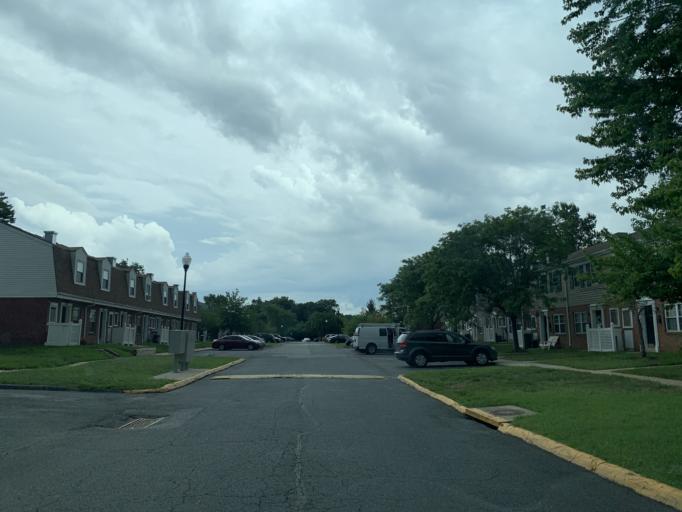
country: US
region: Maryland
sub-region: Baltimore County
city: Essex
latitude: 39.2966
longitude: -76.4545
